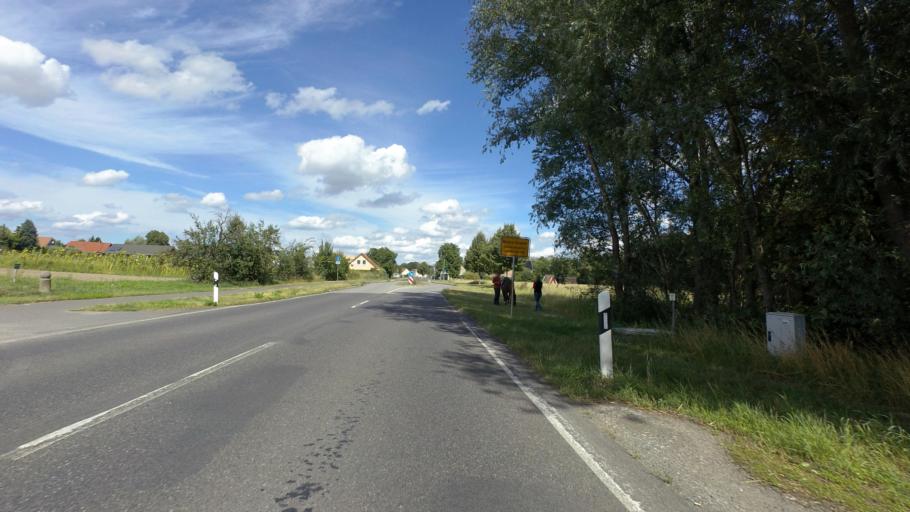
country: DE
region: Brandenburg
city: Wustermark
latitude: 52.5120
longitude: 12.9327
